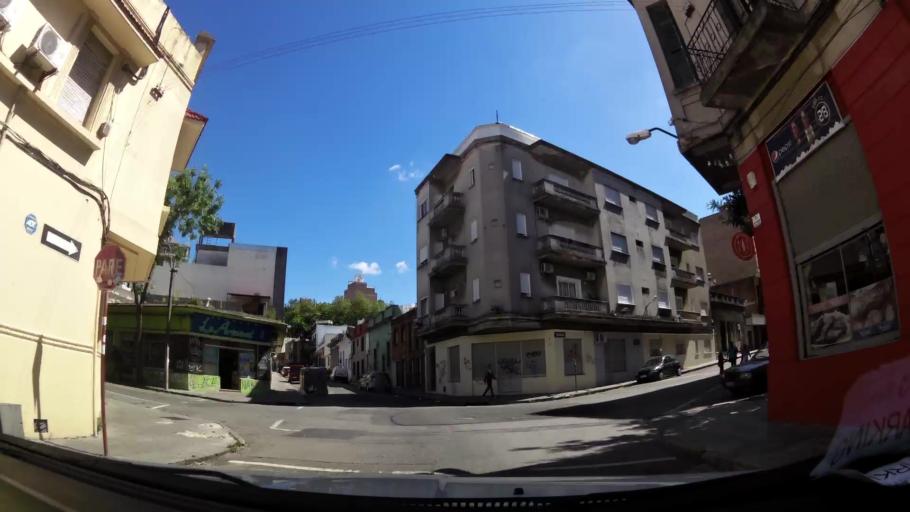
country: UY
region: Montevideo
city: Montevideo
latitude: -34.9057
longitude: -56.1772
